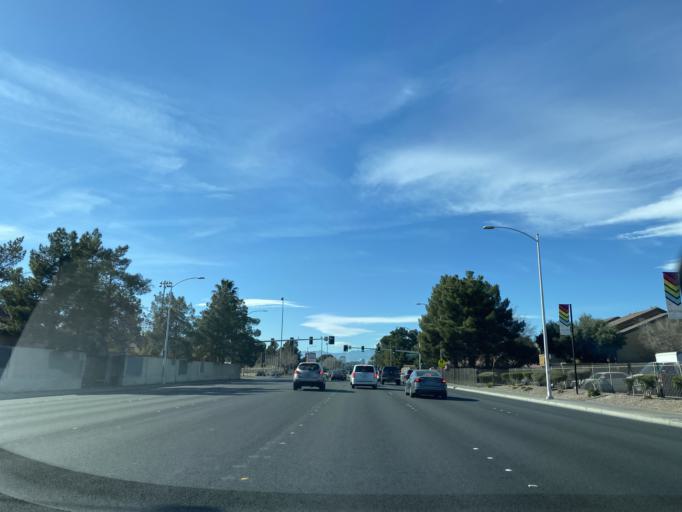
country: US
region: Nevada
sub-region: Clark County
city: North Las Vegas
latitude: 36.1735
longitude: -115.0882
